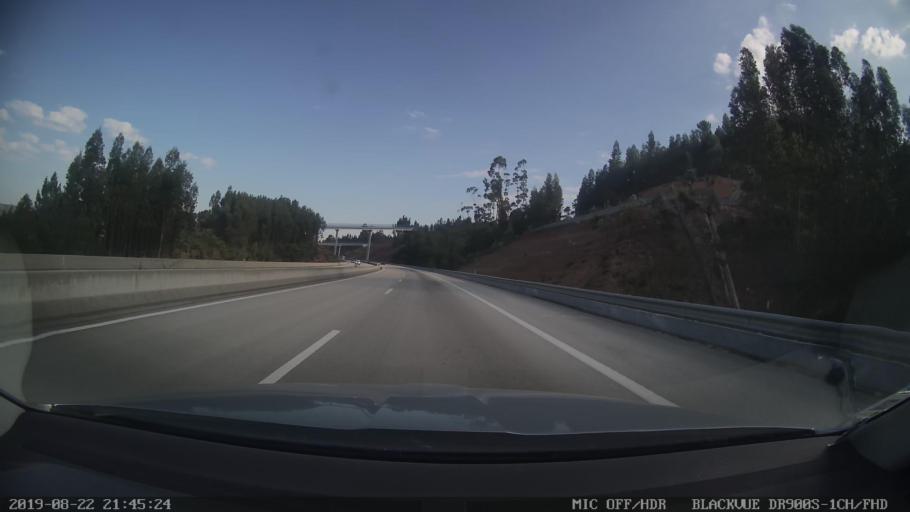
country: PT
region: Coimbra
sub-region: Penela
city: Penela
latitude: 39.9692
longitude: -8.3523
